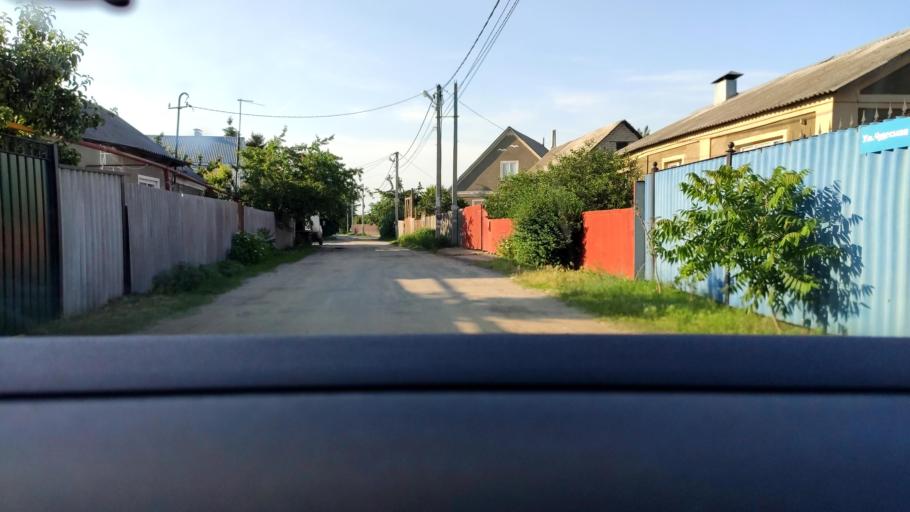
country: RU
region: Voronezj
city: Podgornoye
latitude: 51.7287
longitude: 39.1431
